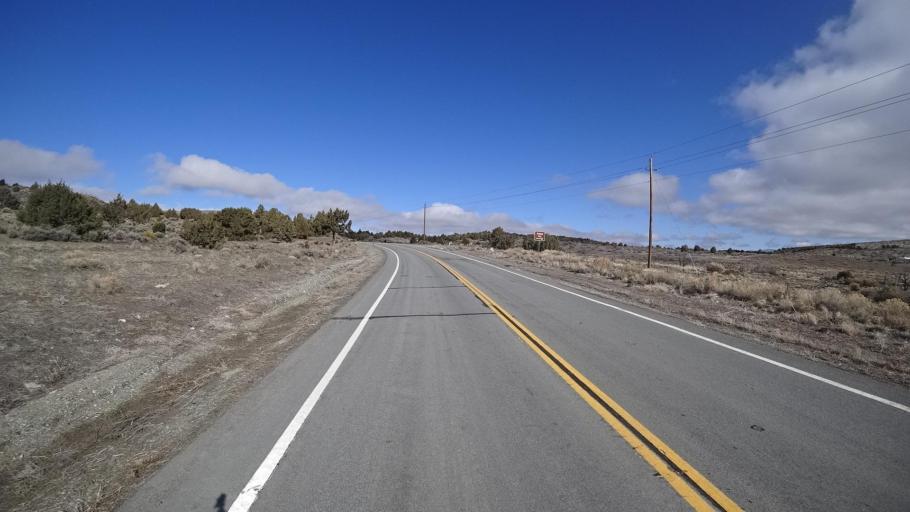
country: US
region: Nevada
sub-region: Washoe County
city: Cold Springs
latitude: 39.7698
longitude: -119.8874
